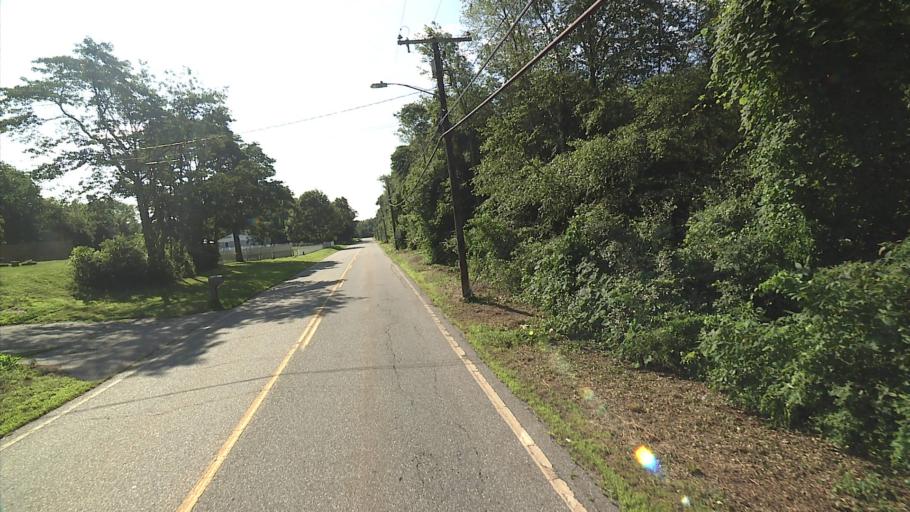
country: US
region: Connecticut
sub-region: New London County
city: Montville Center
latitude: 41.4900
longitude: -72.1731
